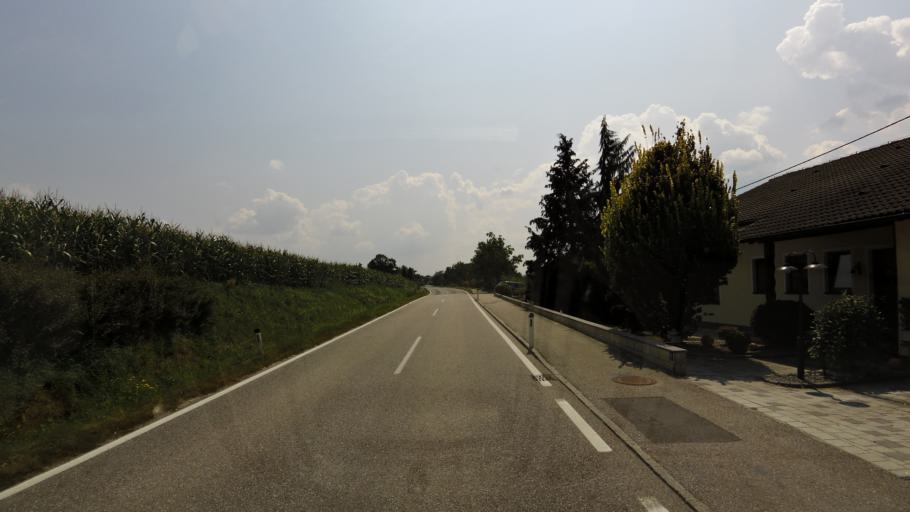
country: AT
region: Upper Austria
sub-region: Politischer Bezirk Ried im Innkreis
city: Waldzell
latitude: 48.2007
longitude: 13.3733
